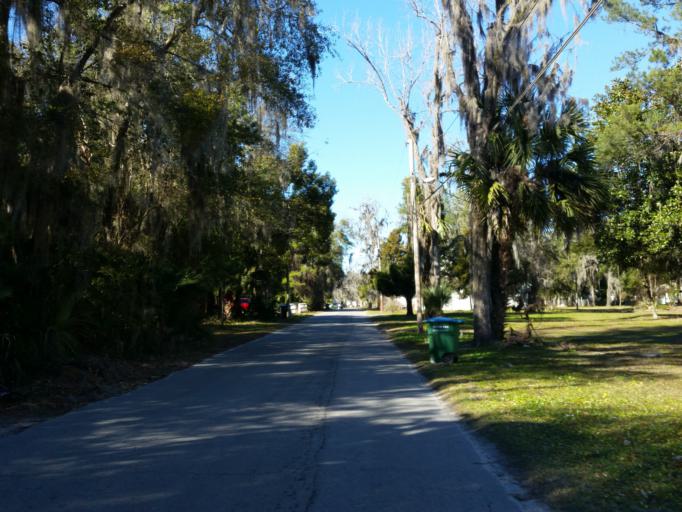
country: US
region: Florida
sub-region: Hamilton County
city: Jasper
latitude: 30.5148
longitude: -82.9514
